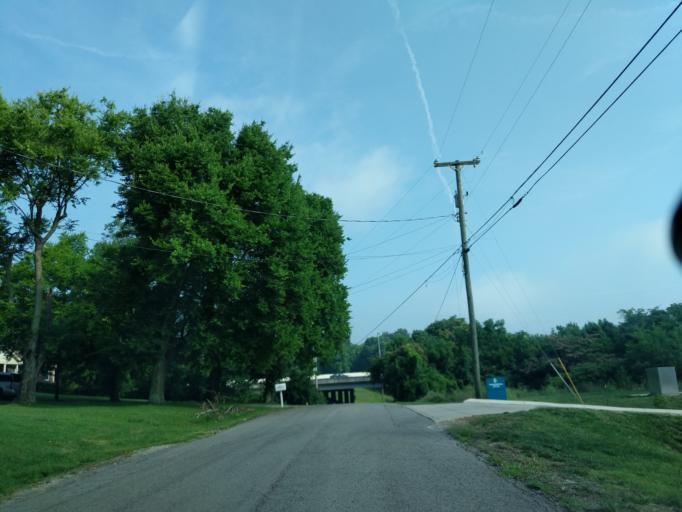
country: US
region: Tennessee
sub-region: Davidson County
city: Goodlettsville
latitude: 36.3075
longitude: -86.6908
